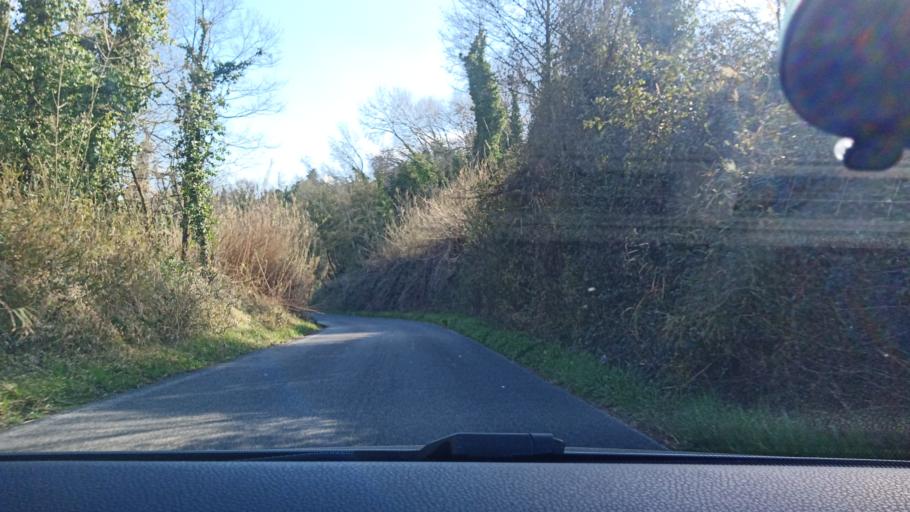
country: IT
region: Latium
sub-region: Citta metropolitana di Roma Capitale
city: Torrita Tiberina
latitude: 42.2435
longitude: 12.6207
